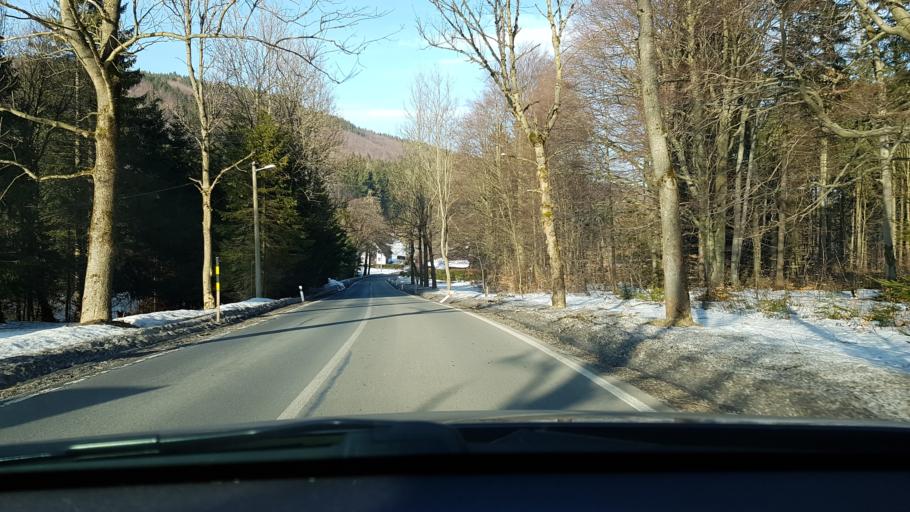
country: CZ
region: Olomoucky
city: Vapenna
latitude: 50.1992
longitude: 17.0674
